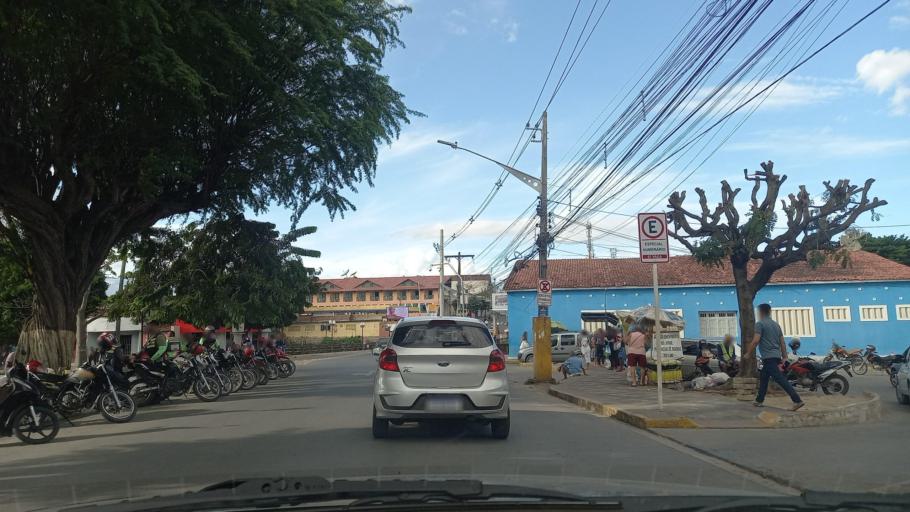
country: BR
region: Pernambuco
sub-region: Gravata
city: Gravata
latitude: -8.2024
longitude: -35.5670
